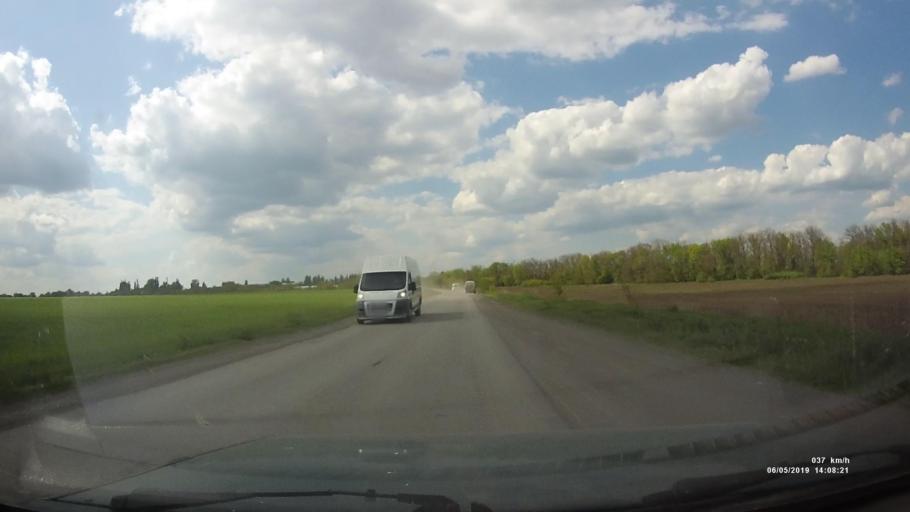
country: RU
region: Rostov
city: Shakhty
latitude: 47.6829
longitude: 40.2987
